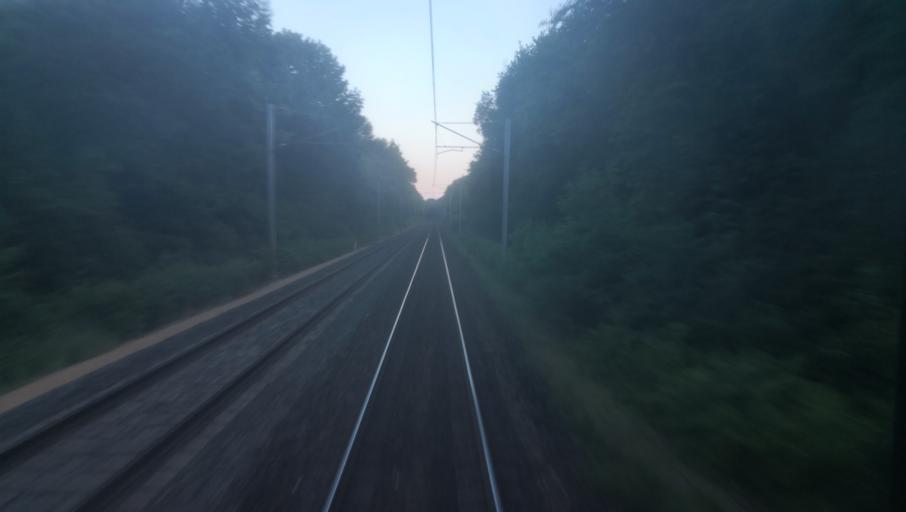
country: FR
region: Centre
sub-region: Departement du Cher
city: Saint-Satur
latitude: 47.3500
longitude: 2.8843
